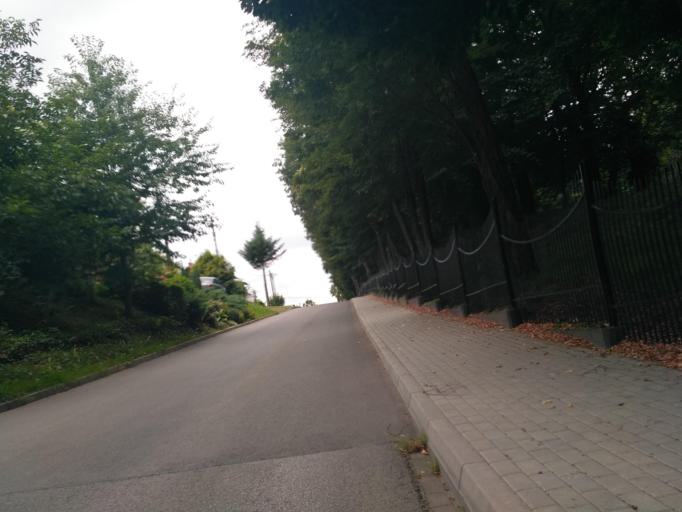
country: PL
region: Subcarpathian Voivodeship
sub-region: Powiat rzeszowski
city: Tyczyn
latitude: 49.9632
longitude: 22.0259
